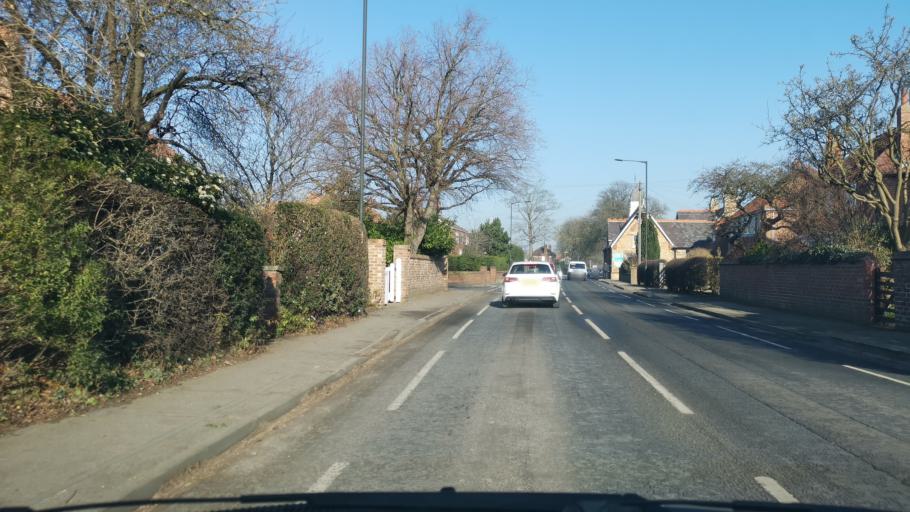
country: GB
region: England
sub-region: City of York
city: Huntington
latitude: 53.9998
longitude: -1.0584
